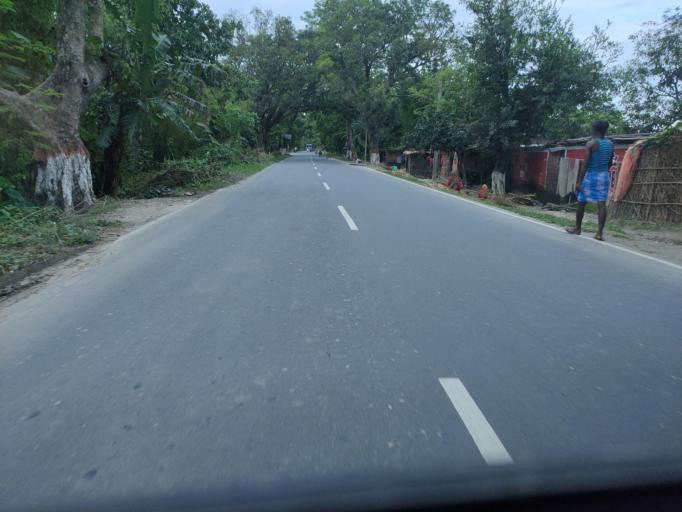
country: IN
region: West Bengal
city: Kishanganj
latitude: 26.1714
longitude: 87.9121
